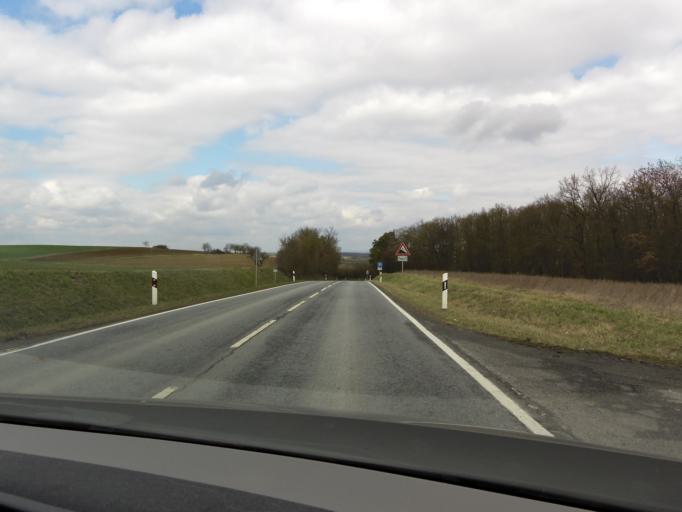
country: DE
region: Bavaria
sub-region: Regierungsbezirk Unterfranken
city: Arnstein
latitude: 49.9647
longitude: 9.9779
